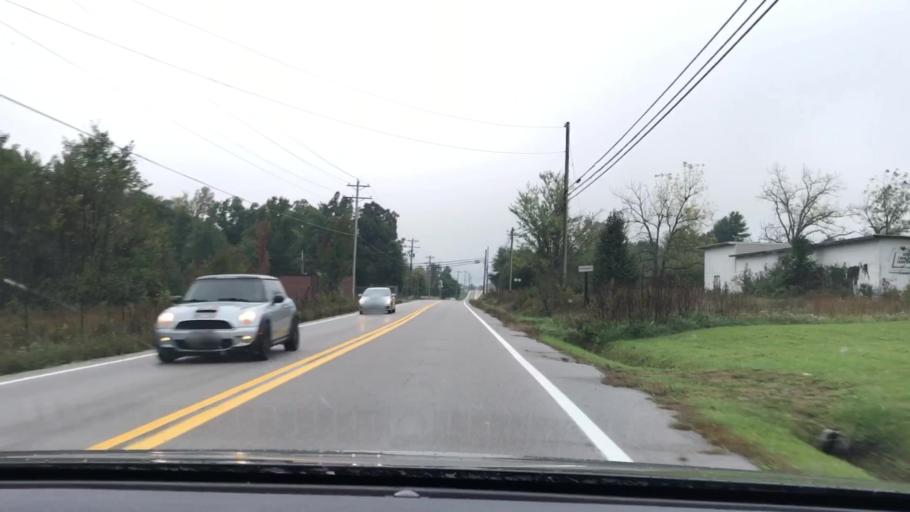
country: US
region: Tennessee
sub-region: Fentress County
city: Grimsley
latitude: 36.2070
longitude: -85.0174
